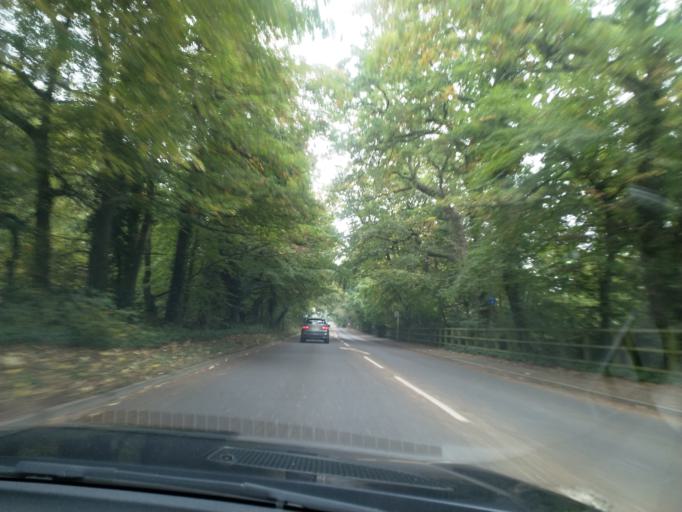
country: GB
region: England
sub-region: Surrey
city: Camberley
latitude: 51.3445
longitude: -0.7284
